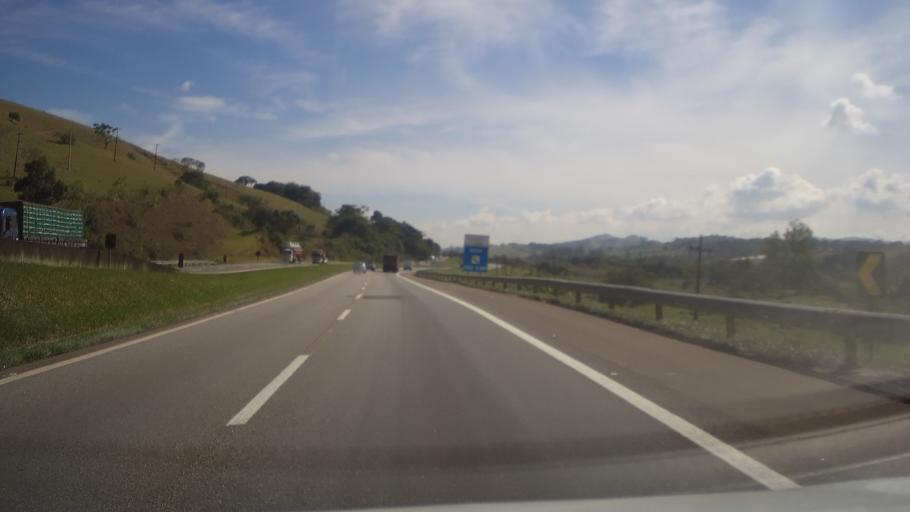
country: BR
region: Minas Gerais
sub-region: Cambui
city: Cambui
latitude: -22.5821
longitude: -46.0458
